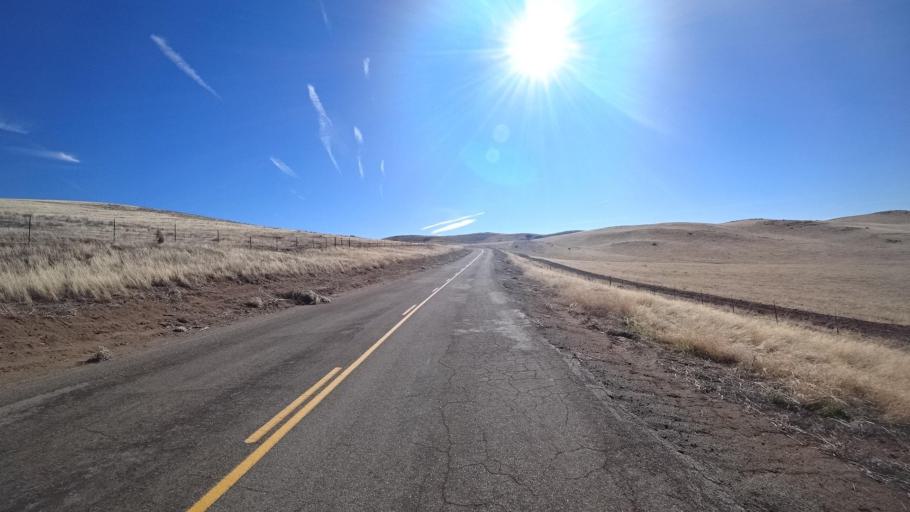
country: US
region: California
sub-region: Kern County
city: Maricopa
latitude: 34.9093
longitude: -119.3938
